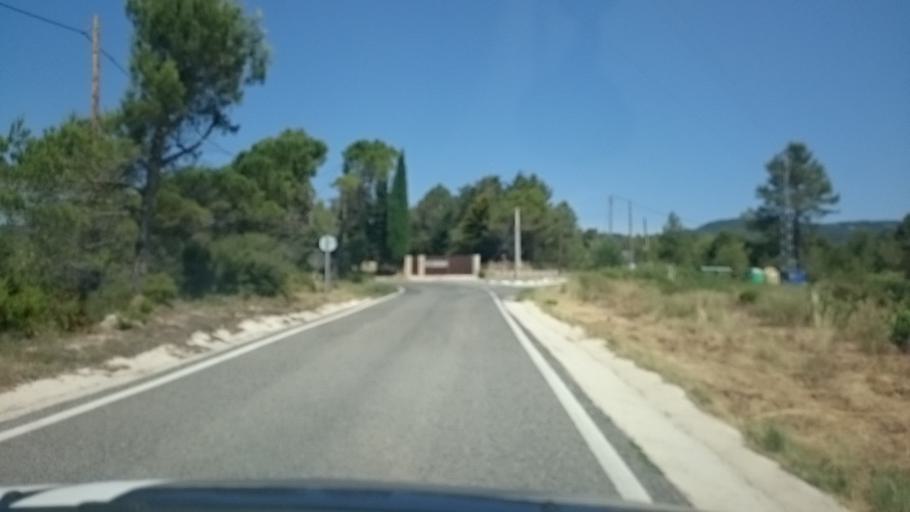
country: ES
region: Catalonia
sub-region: Provincia de Tarragona
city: Querol
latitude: 41.3967
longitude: 1.4515
